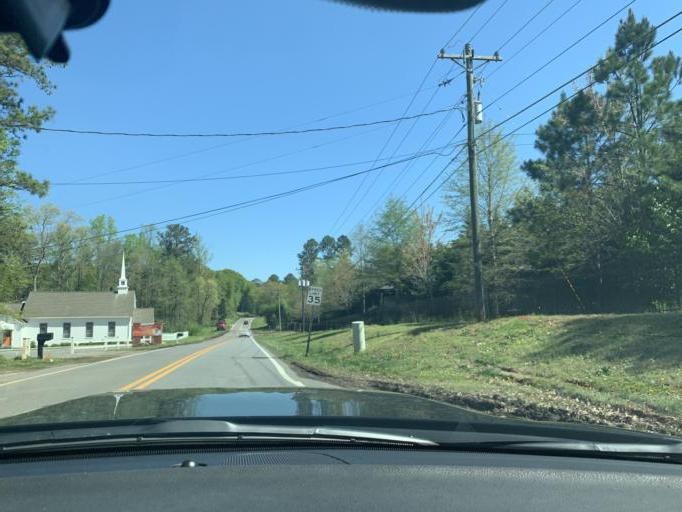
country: US
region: Georgia
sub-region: Fulton County
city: Milton
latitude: 34.1372
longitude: -84.2076
